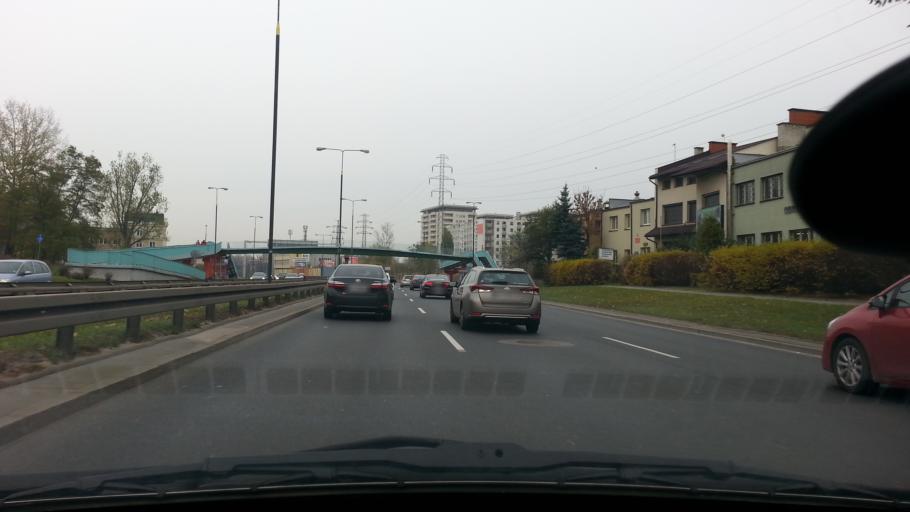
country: PL
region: Masovian Voivodeship
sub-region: Warszawa
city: Wola
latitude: 52.2420
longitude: 20.9577
